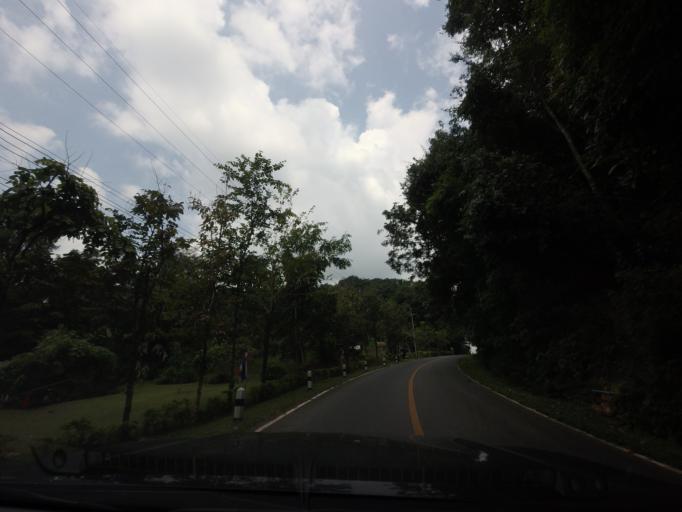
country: TH
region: Nan
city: Pua
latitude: 19.1815
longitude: 100.9729
